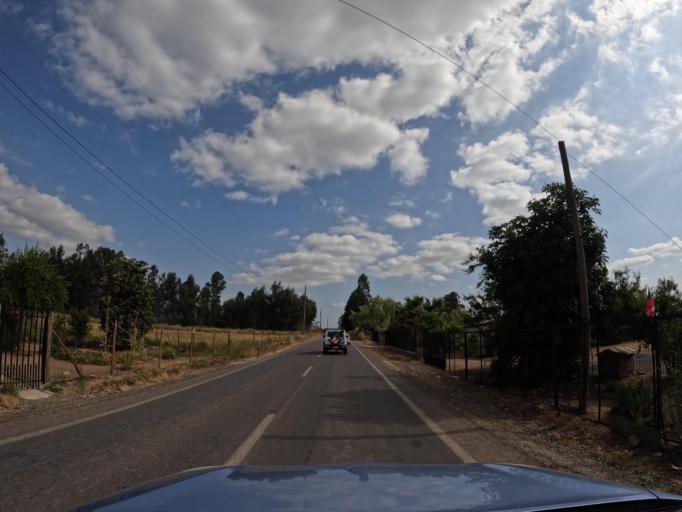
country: CL
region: Maule
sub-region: Provincia de Curico
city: Molina
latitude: -35.1996
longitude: -71.2973
